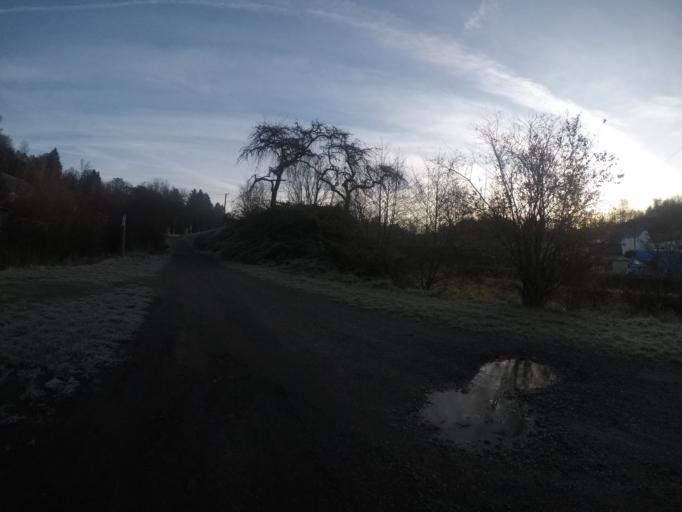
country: BE
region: Wallonia
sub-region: Province du Luxembourg
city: Habay-la-Vieille
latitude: 49.7312
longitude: 5.6514
